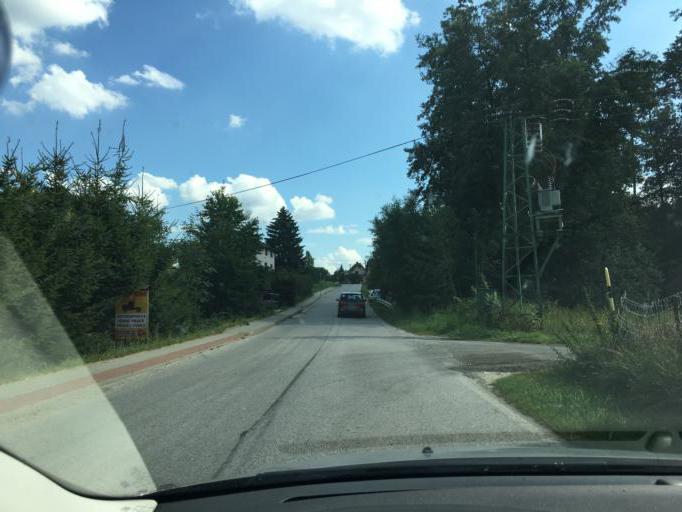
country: CZ
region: Liberecky
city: Zelezny Brod
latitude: 50.6212
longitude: 15.2671
